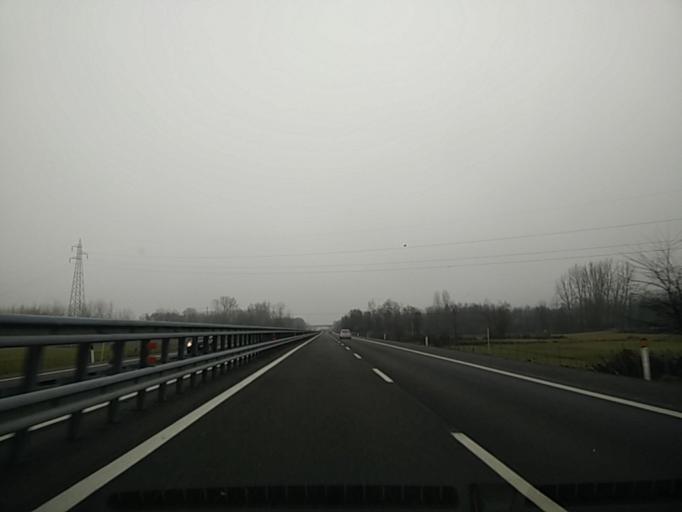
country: IT
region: Piedmont
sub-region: Provincia di Asti
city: Villafranca d'Asti
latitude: 44.9274
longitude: 8.0106
